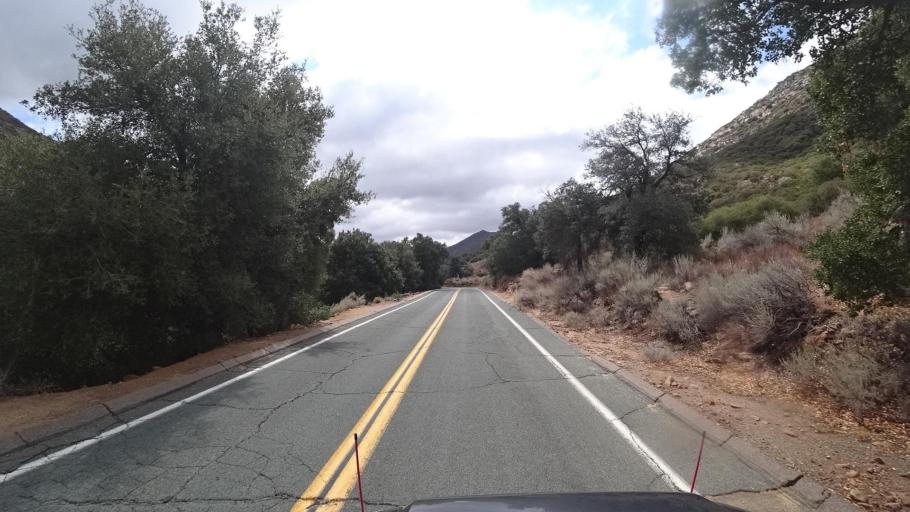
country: US
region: California
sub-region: San Diego County
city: Pine Valley
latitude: 32.7716
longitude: -116.4506
